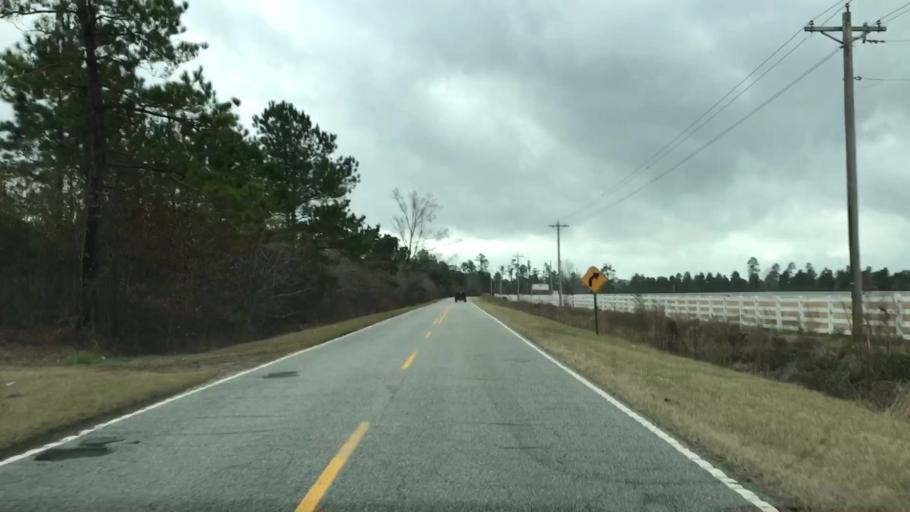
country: US
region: South Carolina
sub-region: Florence County
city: Johnsonville
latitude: 33.6529
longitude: -79.4194
